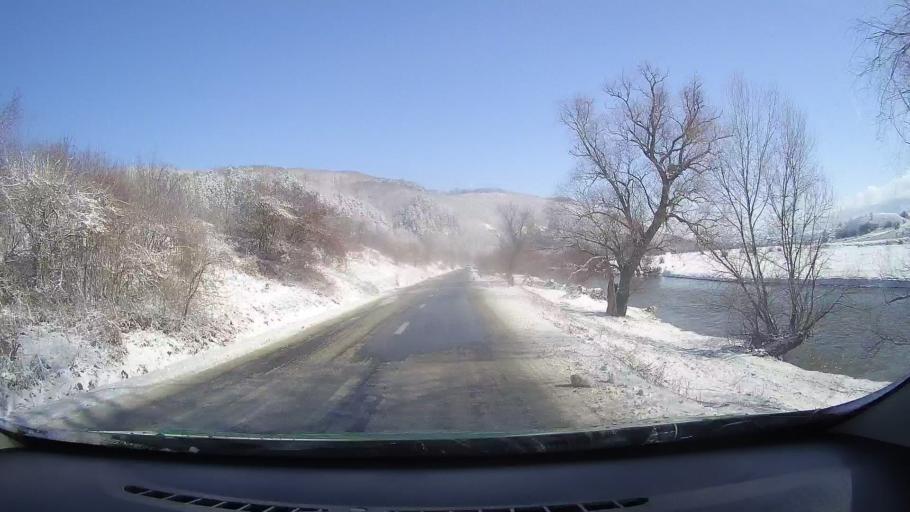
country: RO
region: Sibiu
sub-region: Comuna Talmaciu
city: Talmaciu
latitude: 45.6594
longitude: 24.2773
